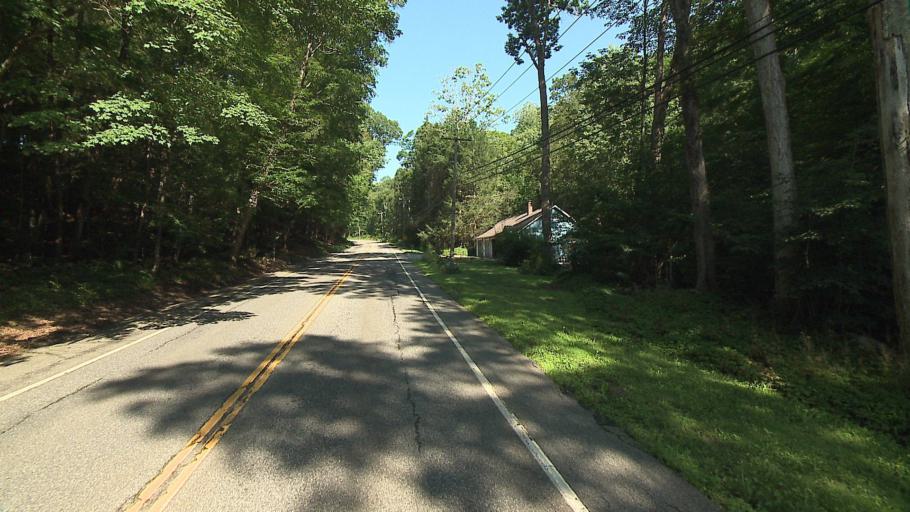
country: US
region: Connecticut
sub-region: Litchfield County
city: Kent
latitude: 41.8251
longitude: -73.4157
